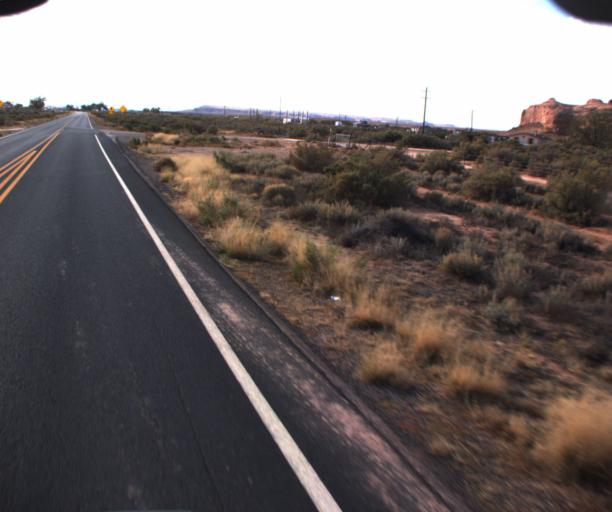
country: US
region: Arizona
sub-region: Apache County
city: Many Farms
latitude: 36.7256
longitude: -109.6299
